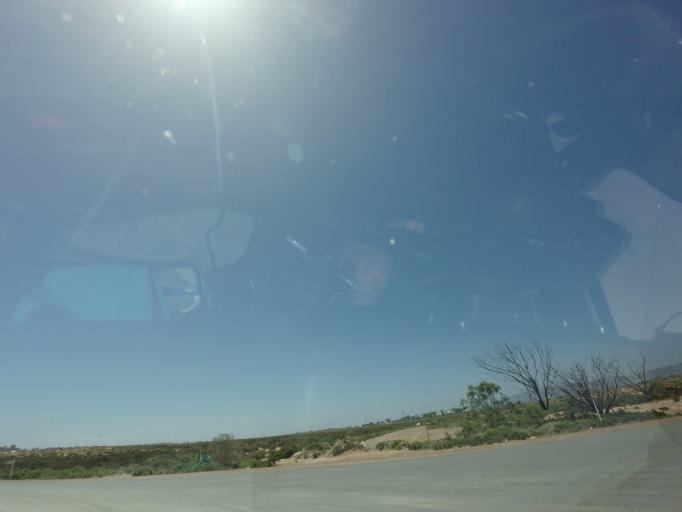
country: AU
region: South Australia
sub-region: Port Augusta
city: Port Augusta
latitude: -32.5081
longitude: 137.7974
